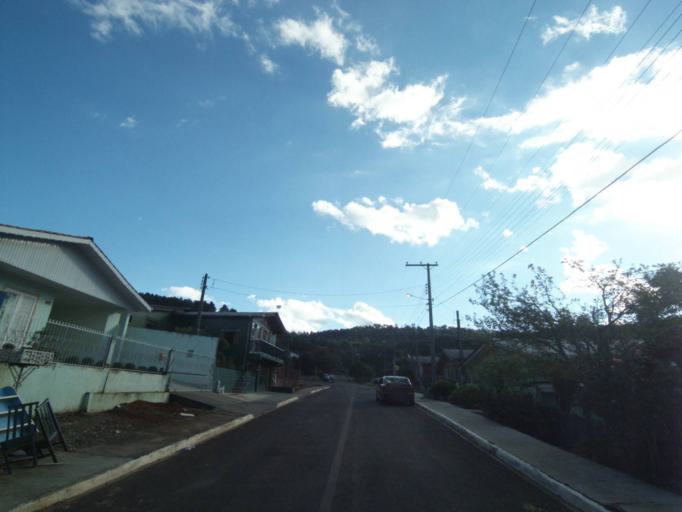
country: BR
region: Parana
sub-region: Uniao Da Vitoria
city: Uniao da Vitoria
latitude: -26.1673
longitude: -51.5357
